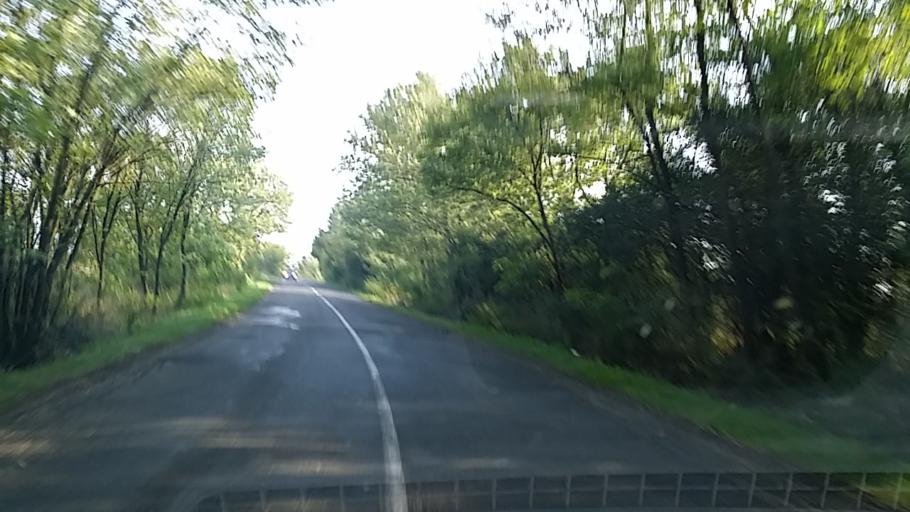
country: HU
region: Nograd
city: Hehalom
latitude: 47.7514
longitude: 19.5775
